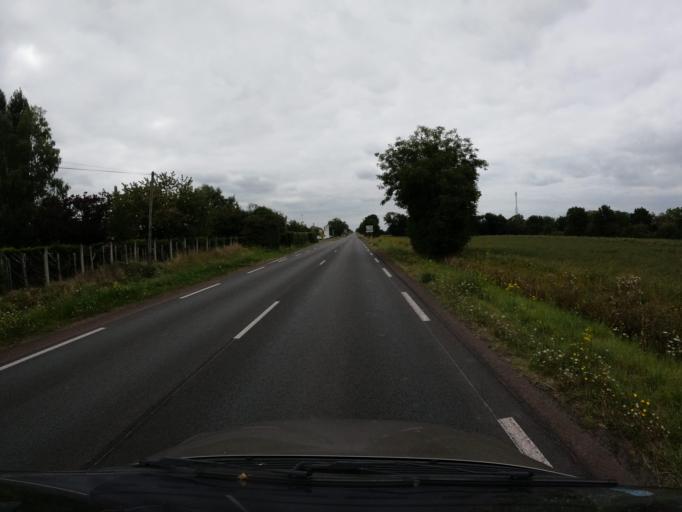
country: FR
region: Pays de la Loire
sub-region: Departement de la Vendee
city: Saint-Michel-le-Cloucq
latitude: 46.4356
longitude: -0.7395
